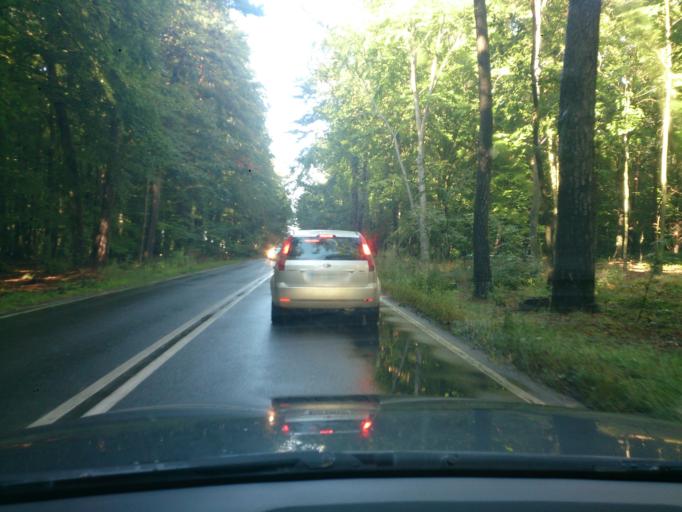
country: PL
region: Pomeranian Voivodeship
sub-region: Gdynia
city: Wielki Kack
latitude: 54.4631
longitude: 18.5087
